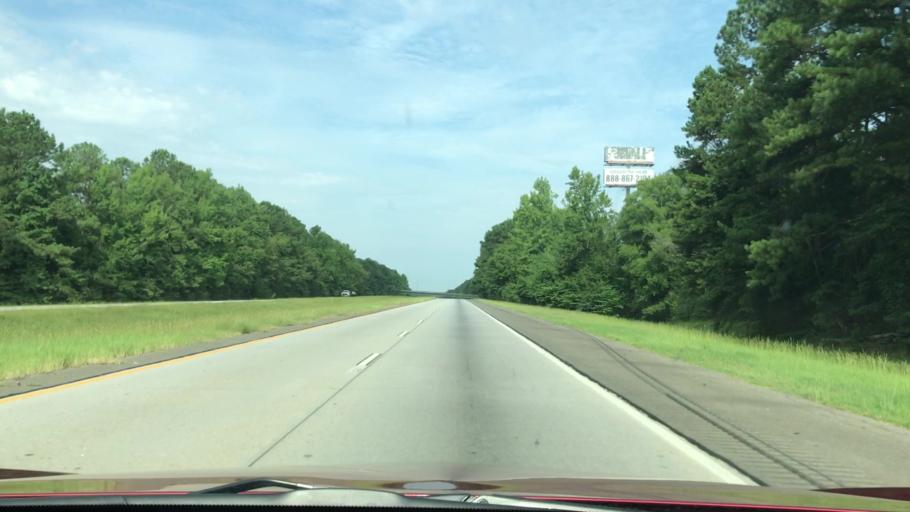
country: US
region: Georgia
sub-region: Warren County
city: Firing Range
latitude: 33.5042
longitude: -82.7429
